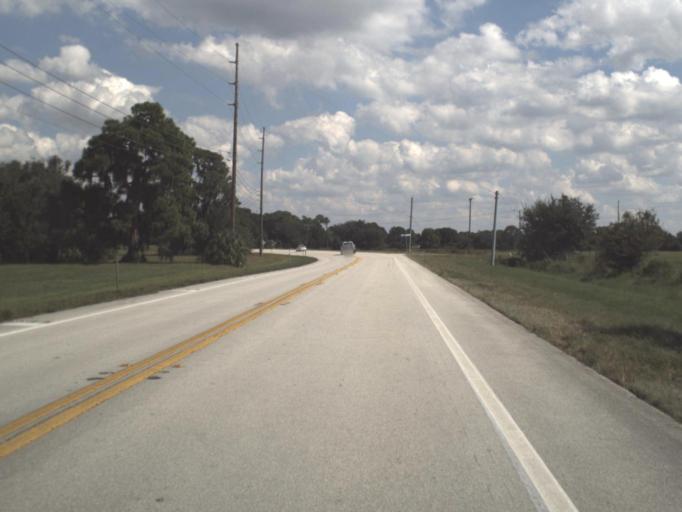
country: US
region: Florida
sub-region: Highlands County
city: Sebring
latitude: 27.4336
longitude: -81.3210
